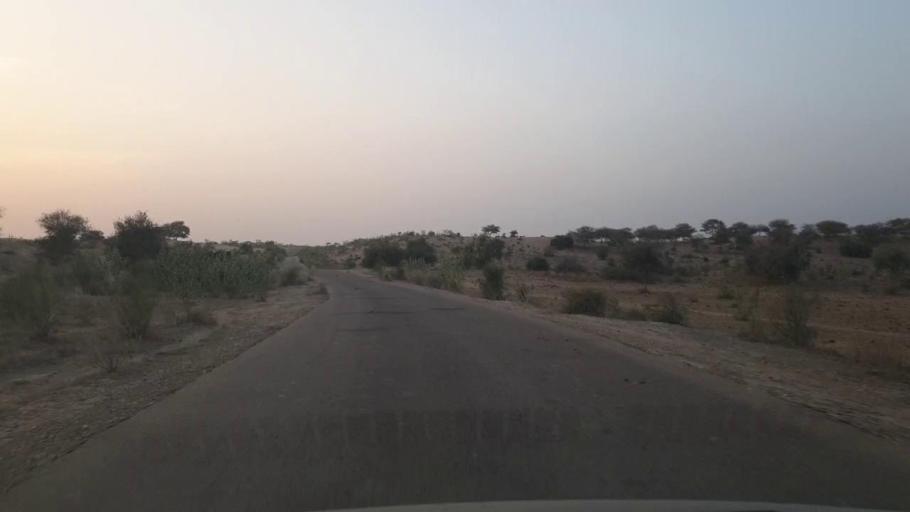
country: PK
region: Sindh
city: Umarkot
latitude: 25.3071
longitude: 70.0701
